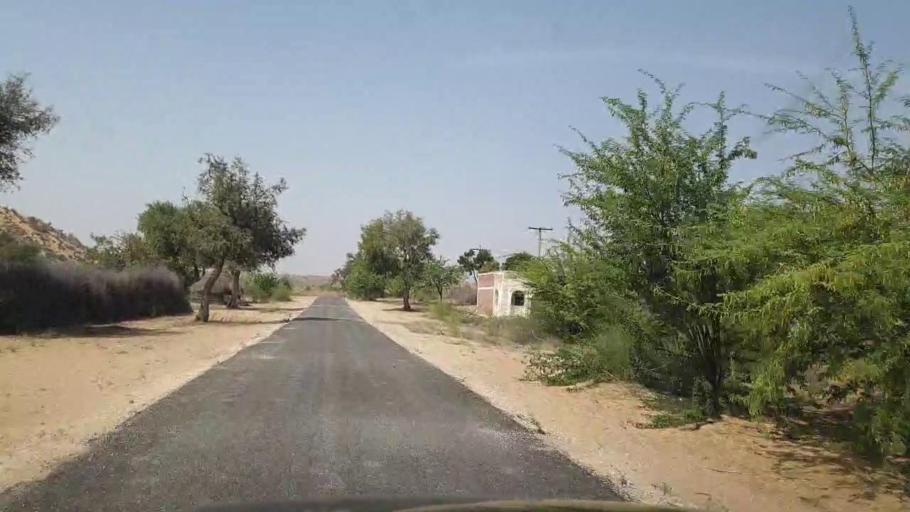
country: PK
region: Sindh
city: Islamkot
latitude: 25.1090
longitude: 70.6521
